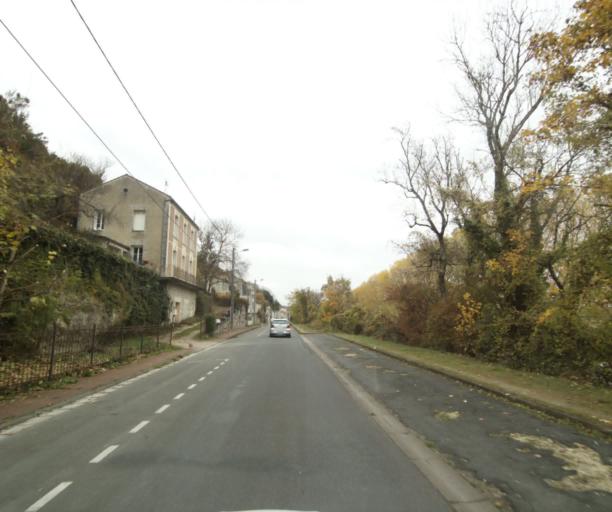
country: FR
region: Poitou-Charentes
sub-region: Departement de la Charente-Maritime
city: Saintes
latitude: 45.7355
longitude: -0.6397
